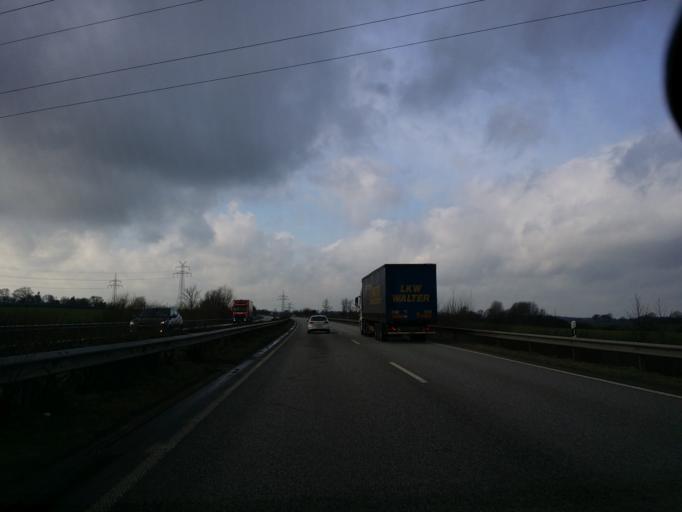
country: DE
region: Schleswig-Holstein
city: Quarnbek
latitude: 54.3154
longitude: 10.0007
